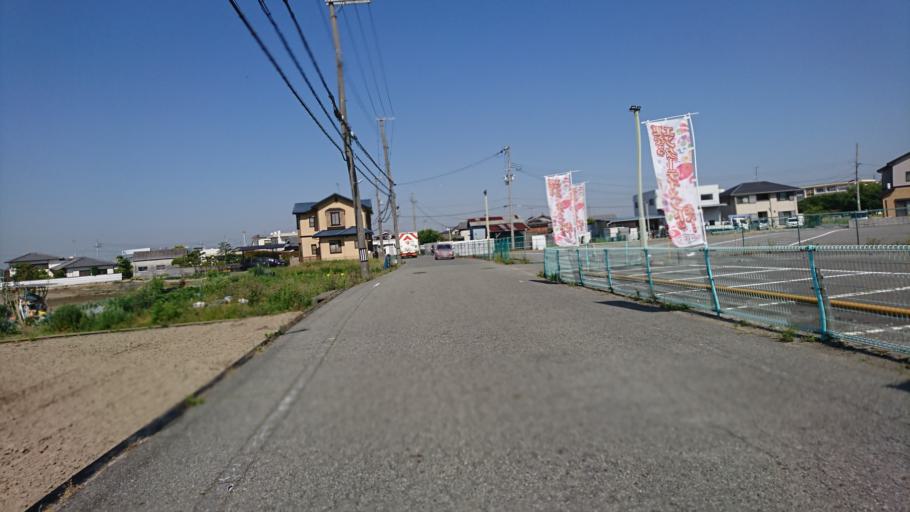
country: JP
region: Hyogo
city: Kakogawacho-honmachi
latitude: 34.7580
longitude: 134.8729
